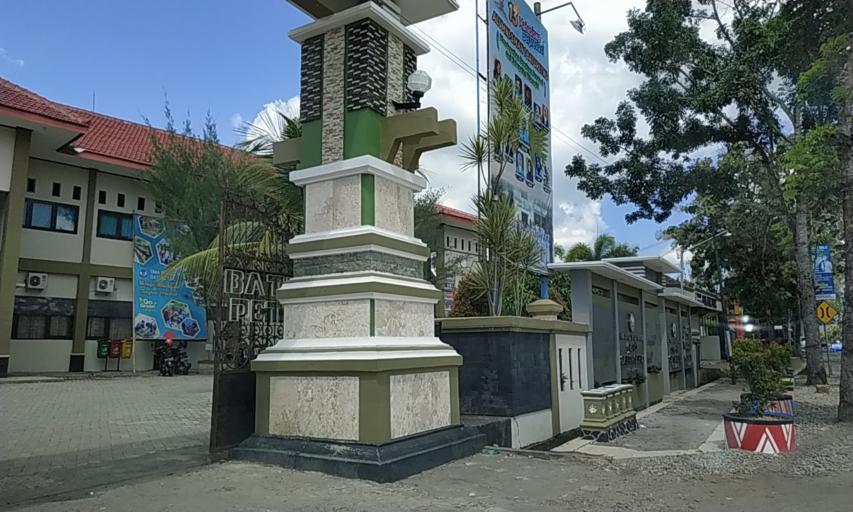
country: ID
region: East Java
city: Ploso
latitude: -7.9946
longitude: 110.9353
